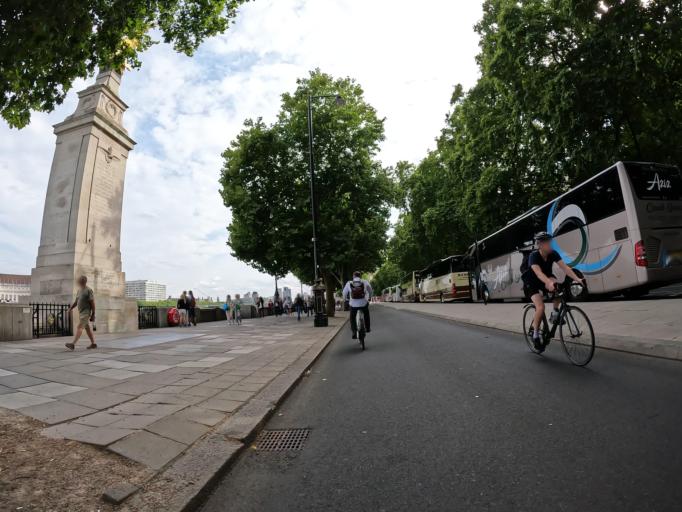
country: GB
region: England
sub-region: Greater London
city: Bromley
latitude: 51.4272
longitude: 0.0160
